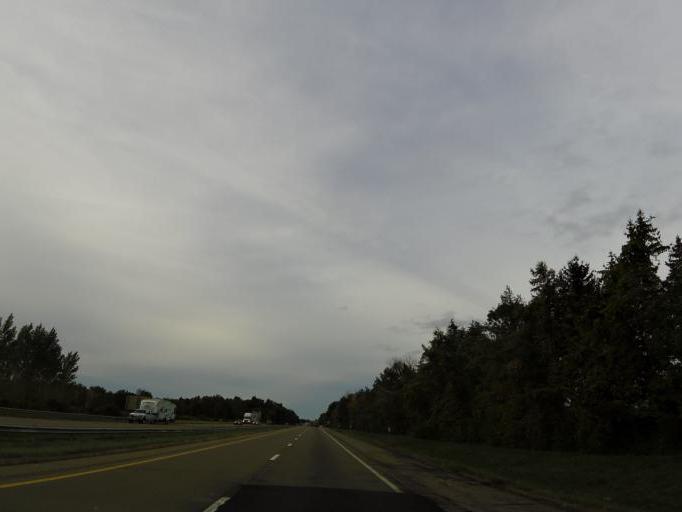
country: US
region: New York
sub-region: Chautauqua County
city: Silver Creek
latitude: 42.5406
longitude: -79.1210
